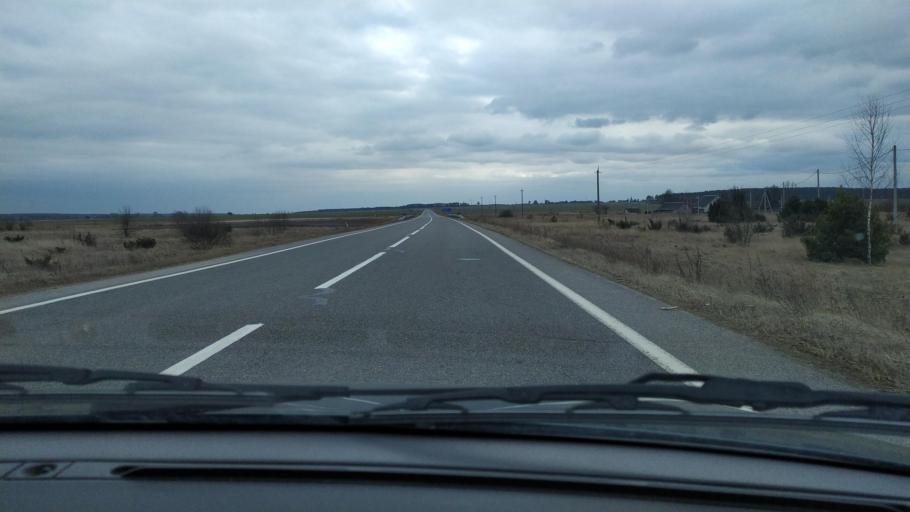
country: BY
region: Brest
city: Kamyanyets
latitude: 52.4228
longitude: 23.8408
